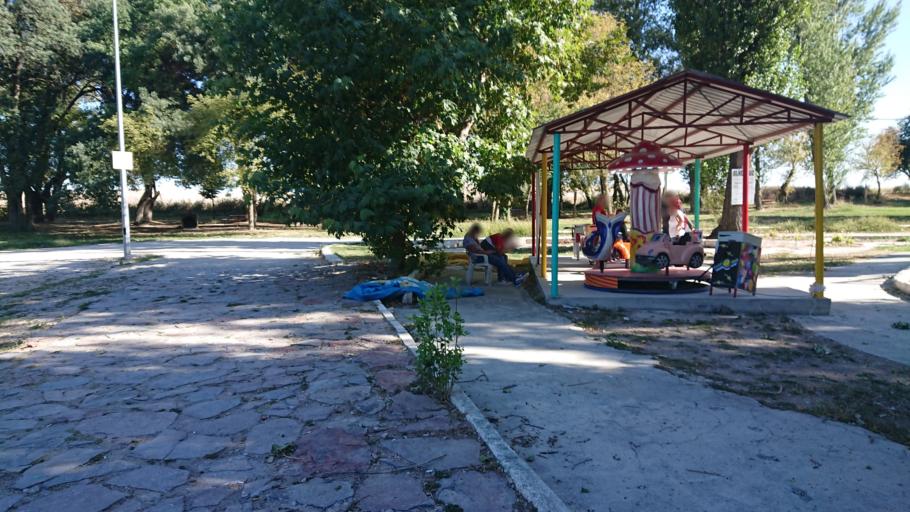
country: TR
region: Eskisehir
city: Cifteler
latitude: 39.3526
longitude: 31.0592
